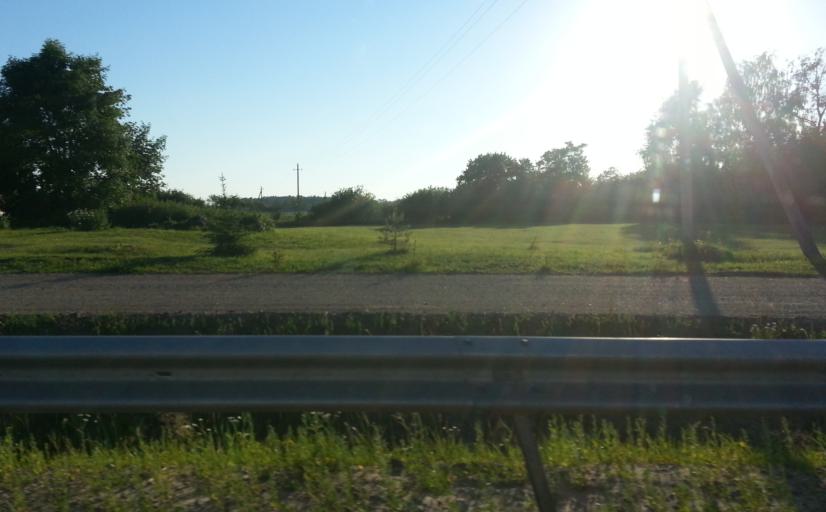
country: LT
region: Panevezys
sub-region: Panevezys City
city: Panevezys
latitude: 55.6213
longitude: 24.3476
